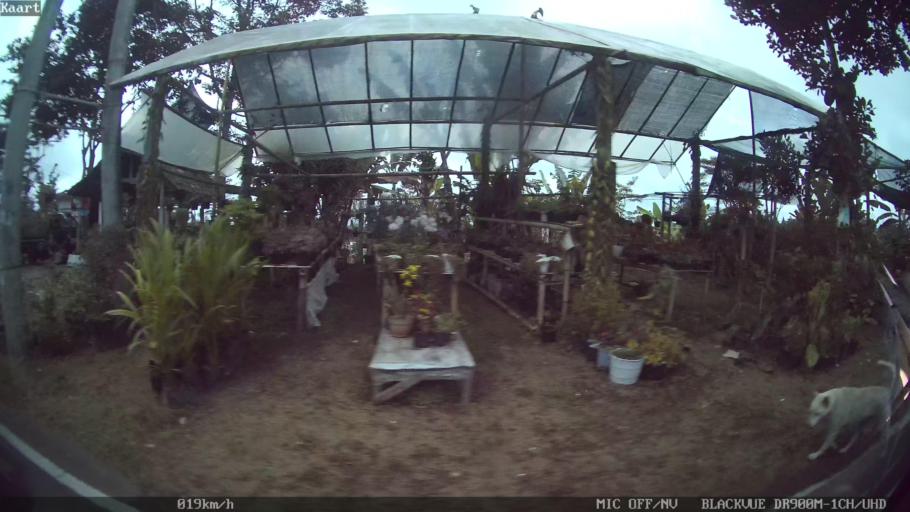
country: ID
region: Bali
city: Banjar Geriana Kangin
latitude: -8.3857
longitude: 115.4455
